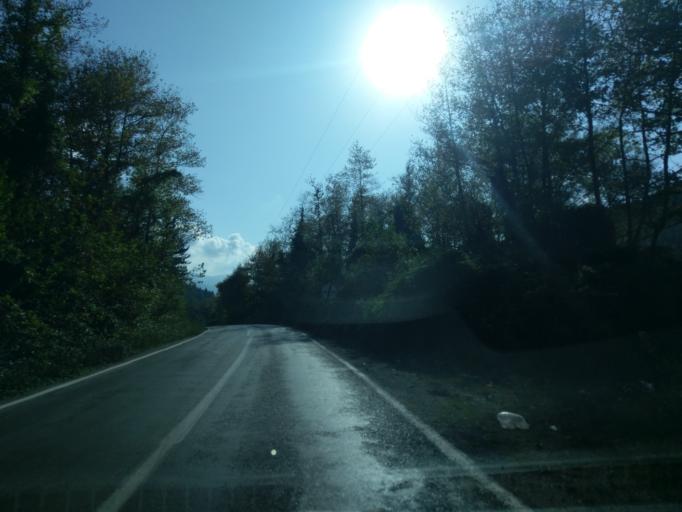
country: TR
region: Sinop
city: Yenikonak
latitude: 41.8858
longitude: 34.5667
